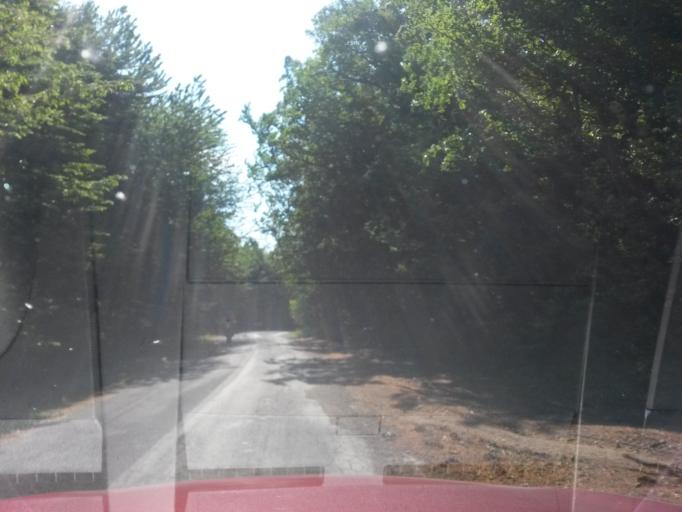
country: SK
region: Kosicky
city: Moldava nad Bodvou
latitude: 48.7226
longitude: 21.0377
